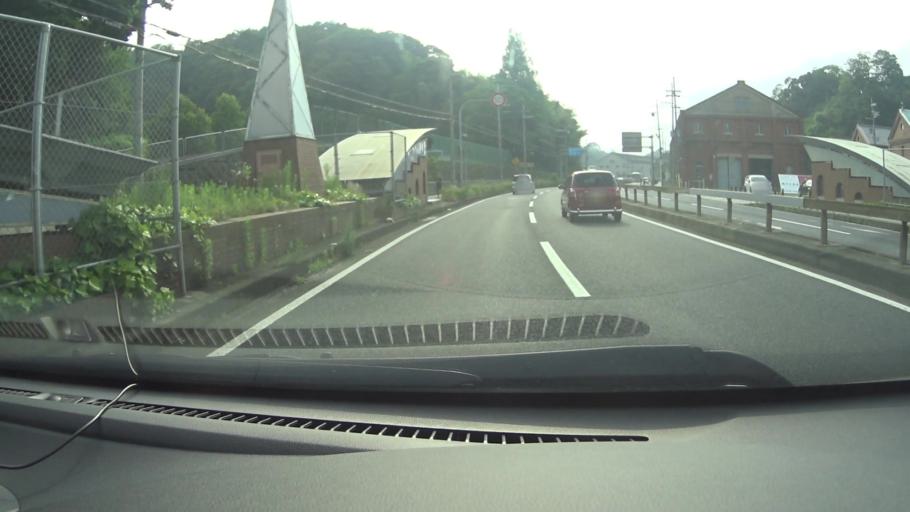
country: JP
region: Kyoto
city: Maizuru
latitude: 35.4739
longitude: 135.3859
